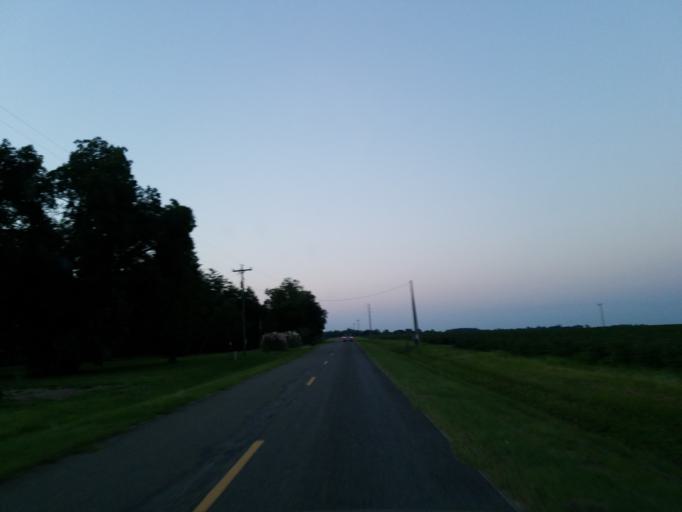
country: US
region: Georgia
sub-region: Dooly County
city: Unadilla
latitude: 32.2732
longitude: -83.7963
